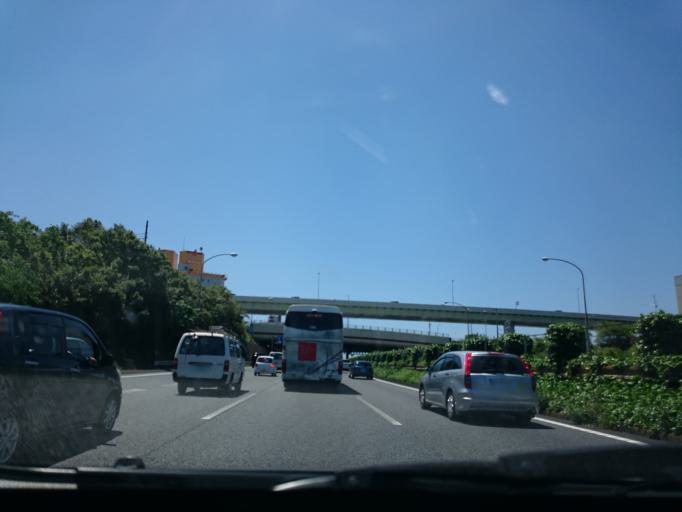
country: JP
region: Kanagawa
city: Minami-rinkan
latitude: 35.5067
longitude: 139.4832
